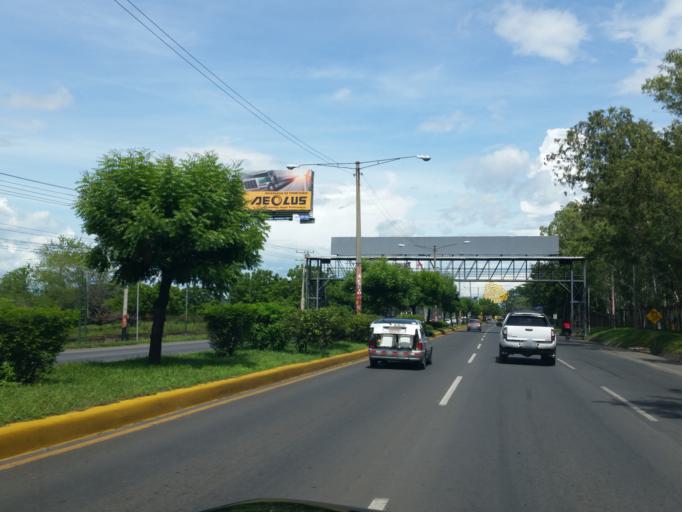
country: NI
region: Managua
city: Managua
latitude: 12.1467
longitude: -86.1834
